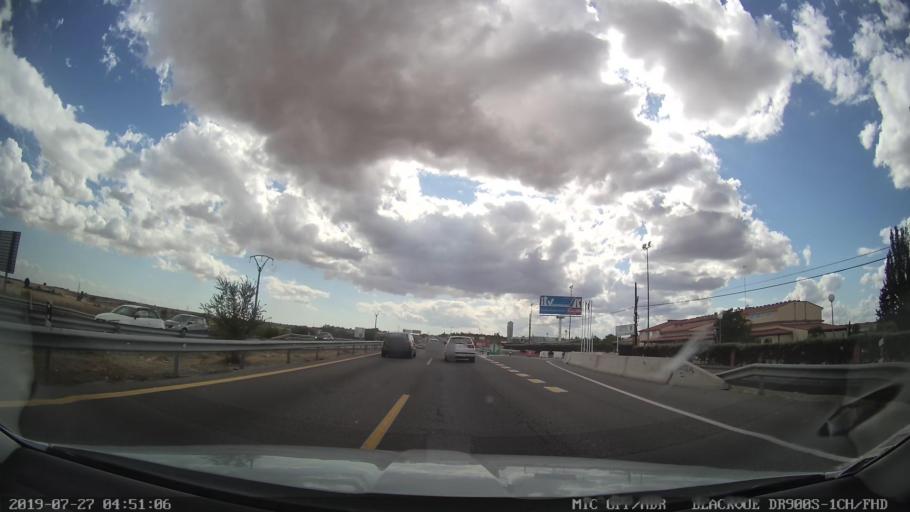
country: ES
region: Madrid
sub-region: Provincia de Madrid
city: Navalcarnero
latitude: 40.2939
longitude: -3.9770
